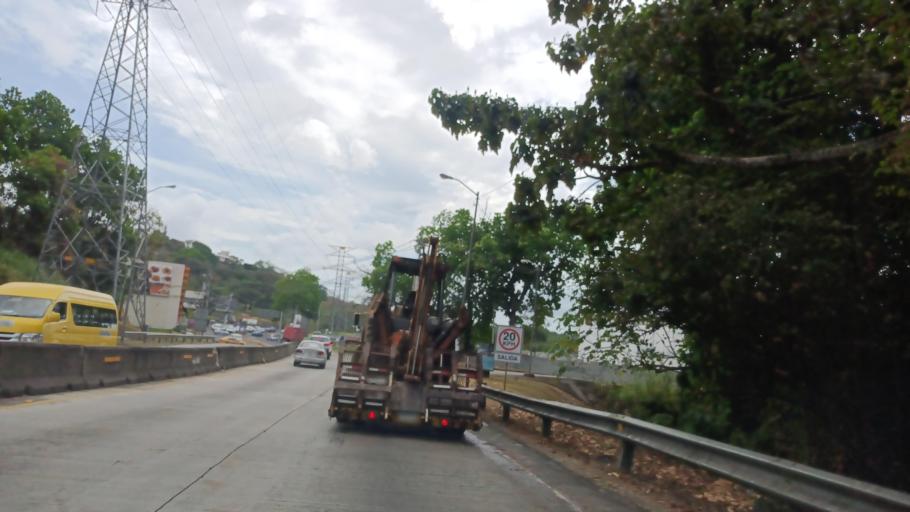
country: PA
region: Panama
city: San Miguelito
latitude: 9.0713
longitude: -79.4625
